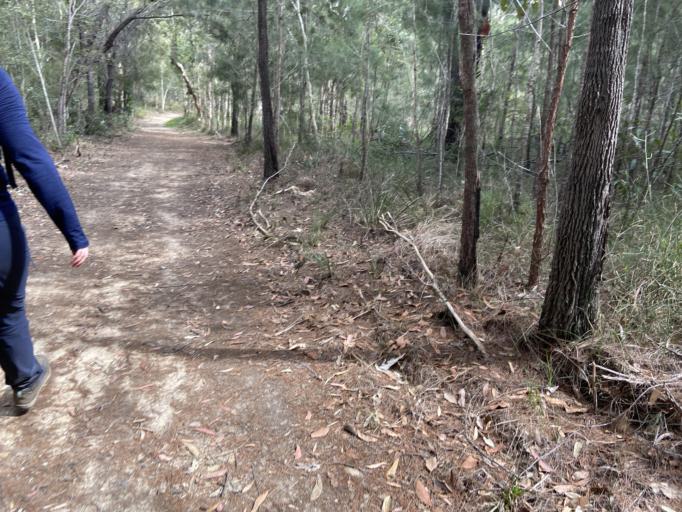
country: AU
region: Queensland
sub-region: Moreton Bay
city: Caboolture
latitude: -26.9502
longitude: 152.9558
